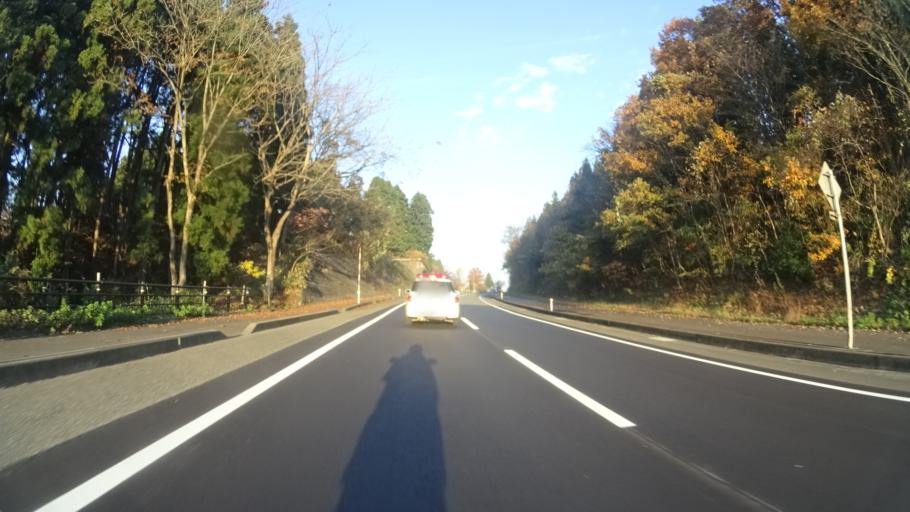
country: JP
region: Niigata
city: Nagaoka
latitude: 37.4491
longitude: 138.7465
